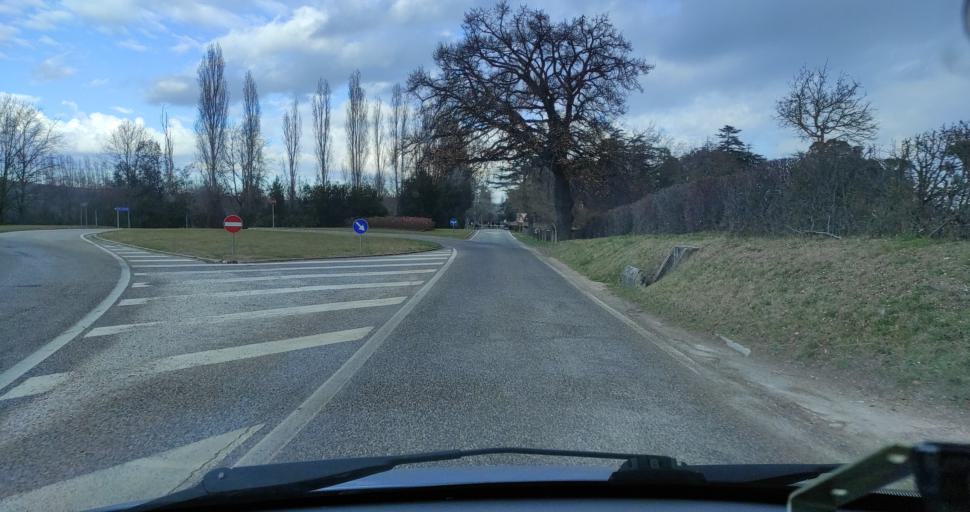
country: IT
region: The Marches
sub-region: Provincia di Macerata
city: Casette Verdini
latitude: 43.2190
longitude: 13.4058
